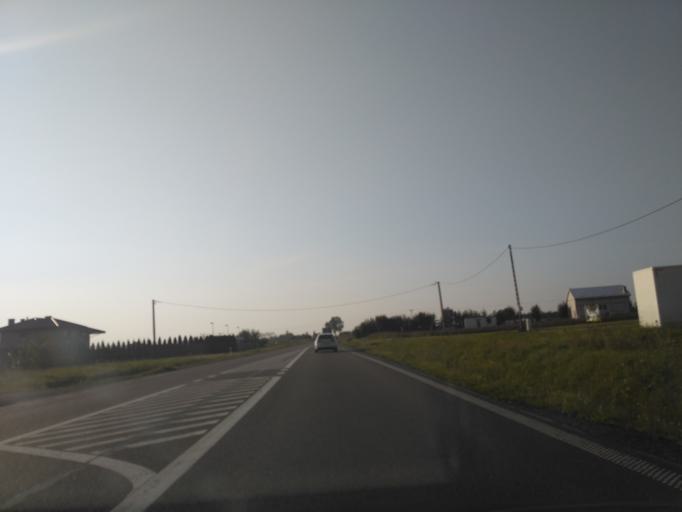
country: PL
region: Lublin Voivodeship
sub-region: Powiat janowski
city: Modliborzyce
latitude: 50.7451
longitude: 22.3418
